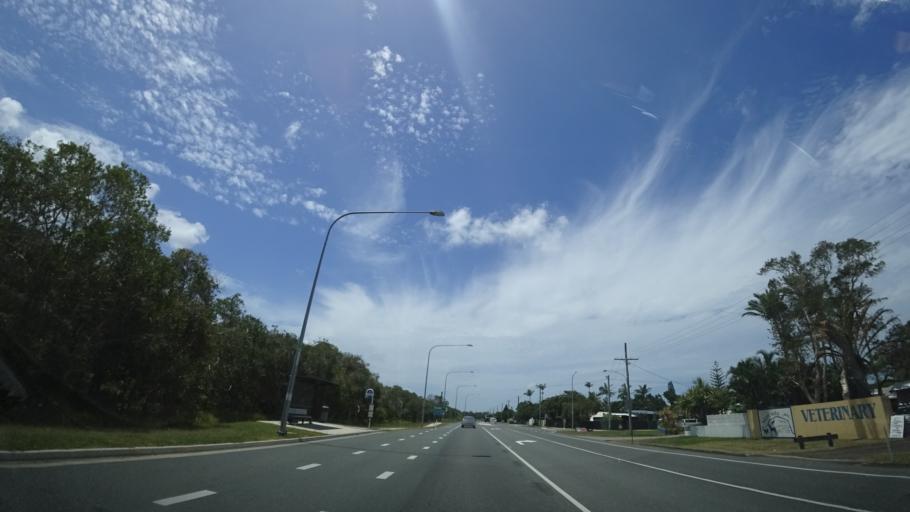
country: AU
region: Queensland
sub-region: Sunshine Coast
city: Coolum Beach
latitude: -26.5851
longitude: 153.0931
